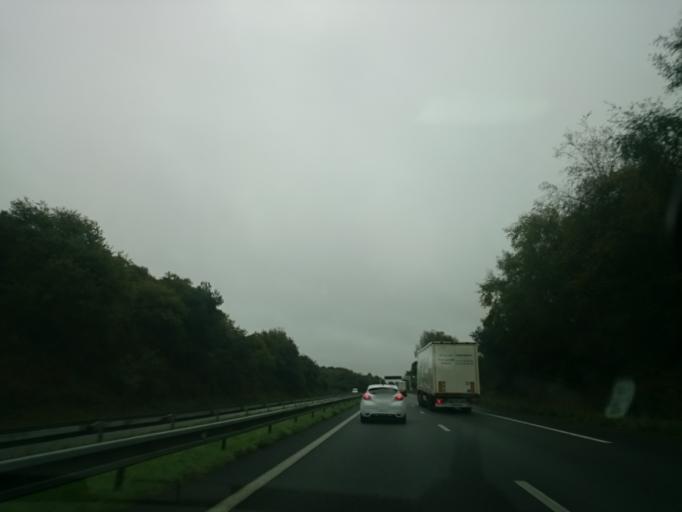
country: FR
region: Brittany
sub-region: Departement du Morbihan
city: Gestel
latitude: 47.7905
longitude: -3.4426
